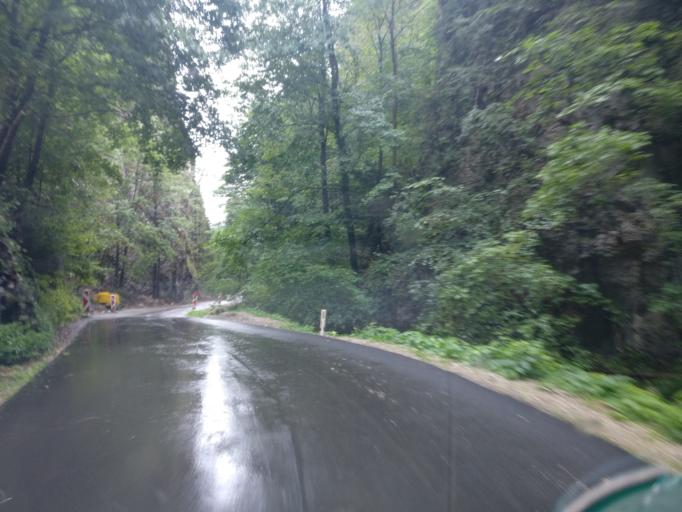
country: AT
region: Lower Austria
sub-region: Politischer Bezirk Neunkirchen
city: Schottwien
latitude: 47.6585
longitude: 15.8471
